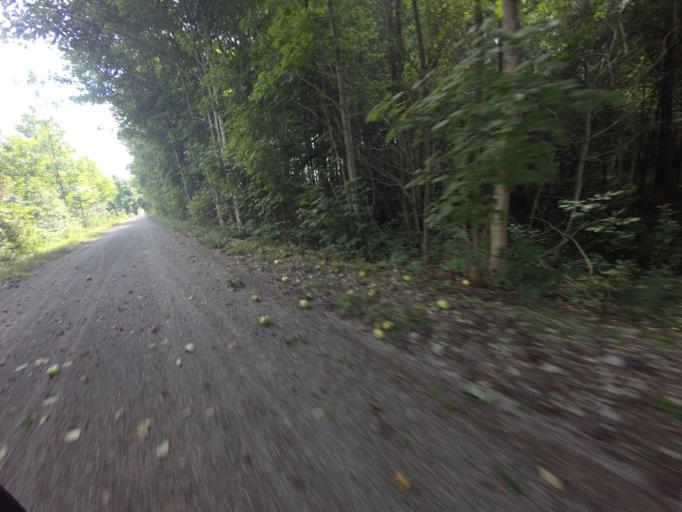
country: CA
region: Ontario
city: Huron East
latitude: 43.6479
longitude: -81.2212
